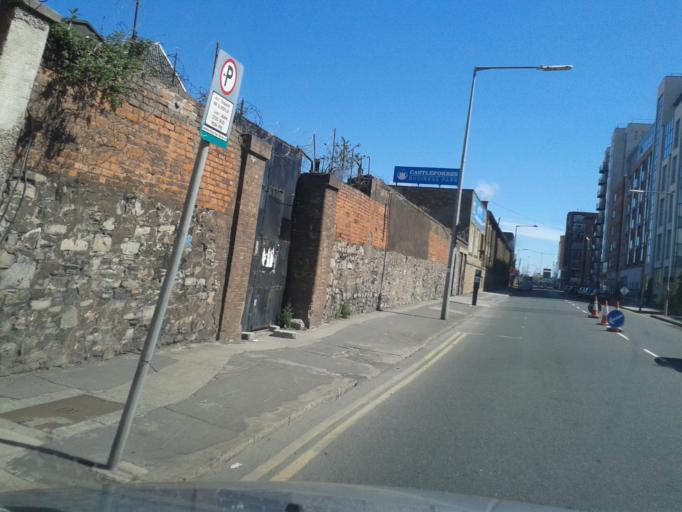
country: IE
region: Leinster
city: Ringsend
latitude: 53.3502
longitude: -6.2341
